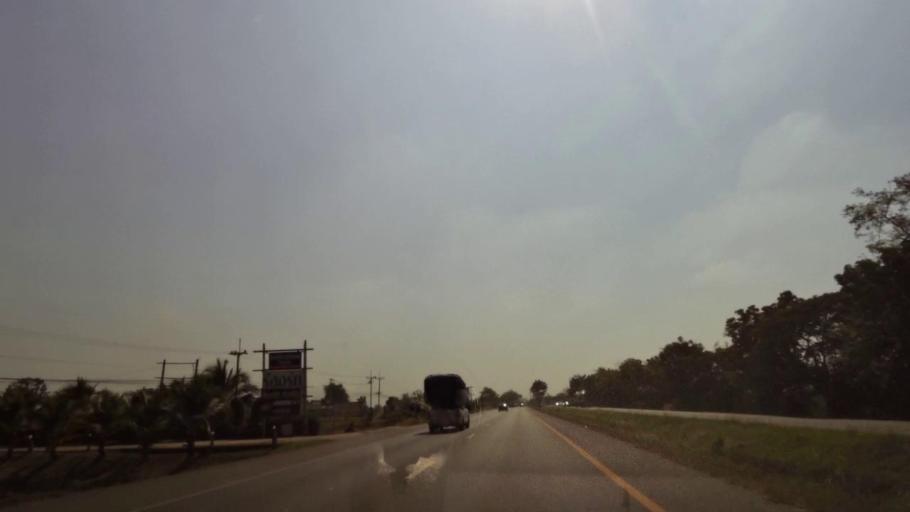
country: TH
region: Phichit
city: Wachira Barami
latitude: 16.4753
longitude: 100.1472
